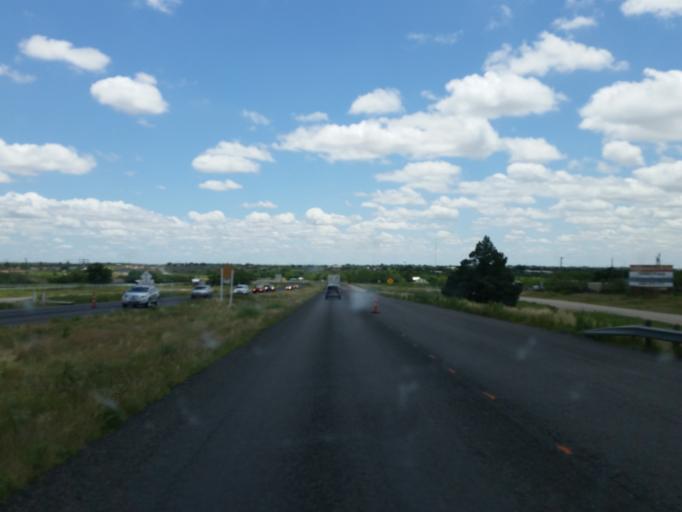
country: US
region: Texas
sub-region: Scurry County
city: Snyder
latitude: 32.7382
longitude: -100.9172
